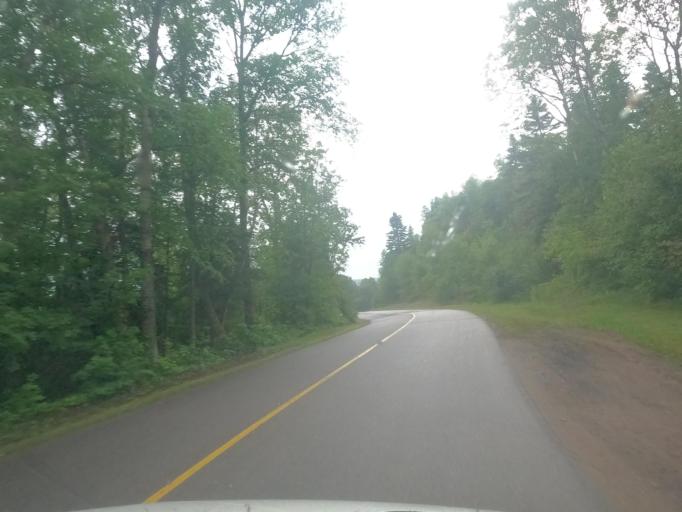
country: CA
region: Ontario
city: Marathon
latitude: 48.7783
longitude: -87.1029
